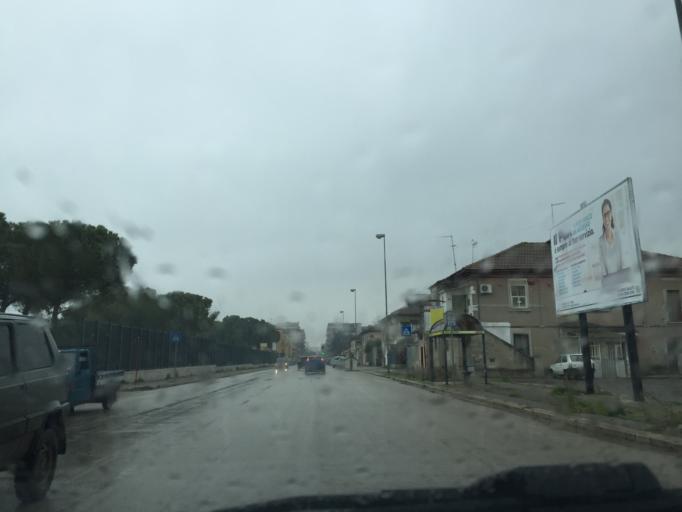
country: IT
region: Apulia
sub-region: Provincia di Foggia
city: Foggia
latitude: 41.4676
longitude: 15.5268
